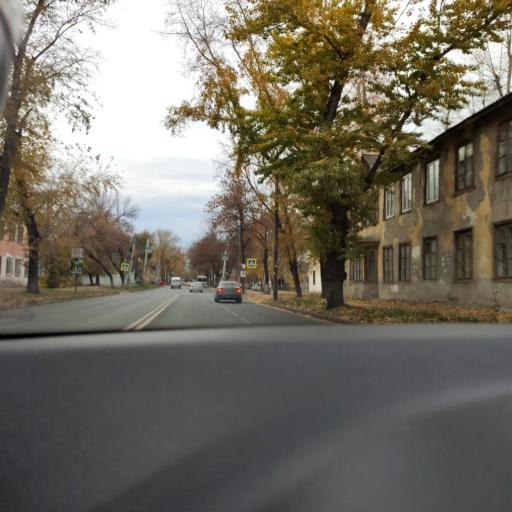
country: RU
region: Samara
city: Samara
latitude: 53.2246
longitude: 50.2596
